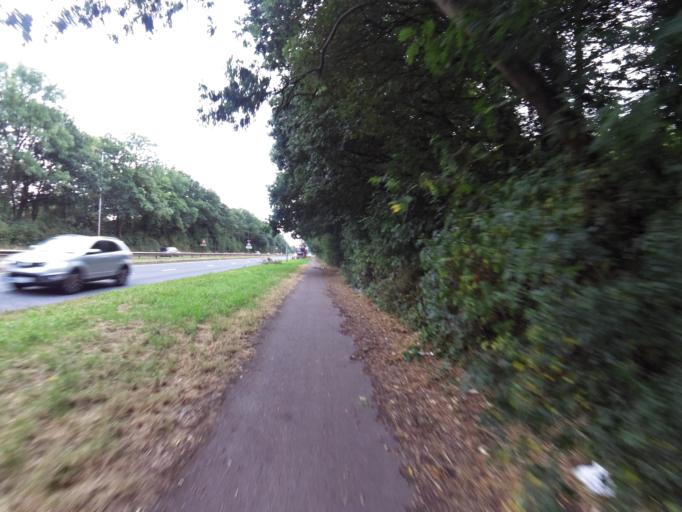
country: GB
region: England
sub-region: Hertfordshire
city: Shenley AV
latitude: 51.7346
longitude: -0.2841
